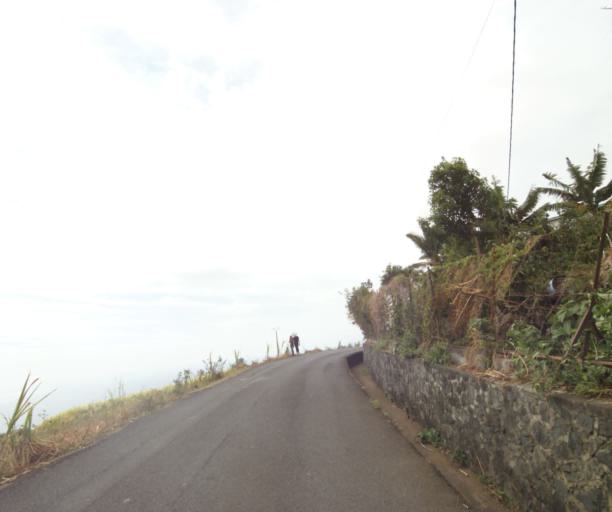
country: RE
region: Reunion
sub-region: Reunion
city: Saint-Paul
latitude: -21.0348
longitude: 55.2900
